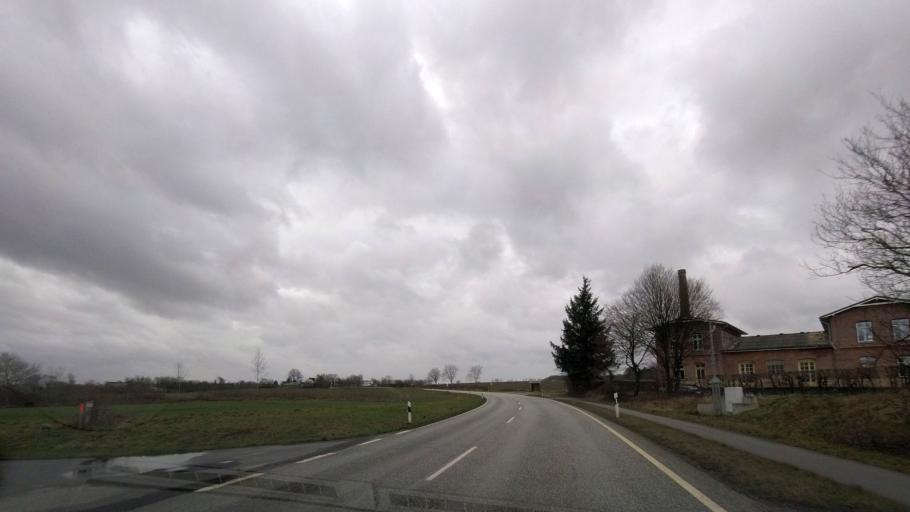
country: DE
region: Schleswig-Holstein
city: Twedt
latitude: 54.6037
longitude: 9.6844
